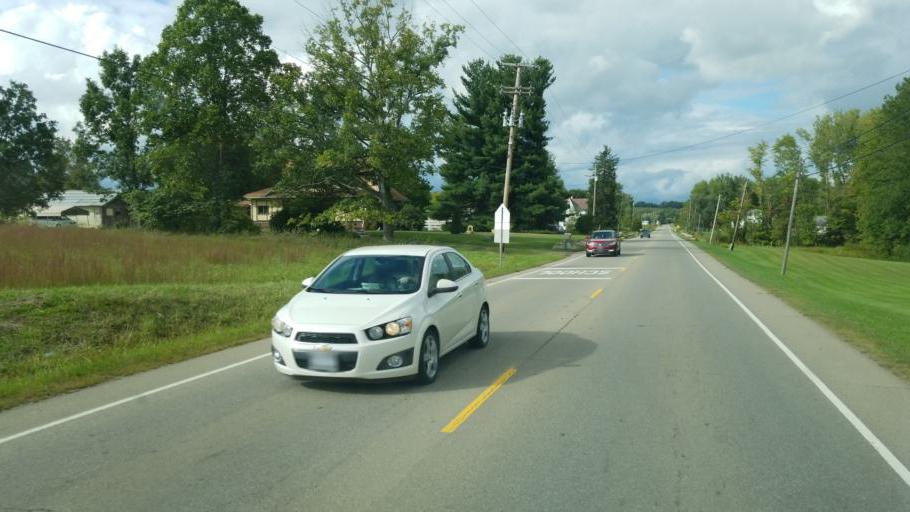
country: US
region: Ohio
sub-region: Jackson County
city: Oak Hill
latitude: 38.9097
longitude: -82.5682
